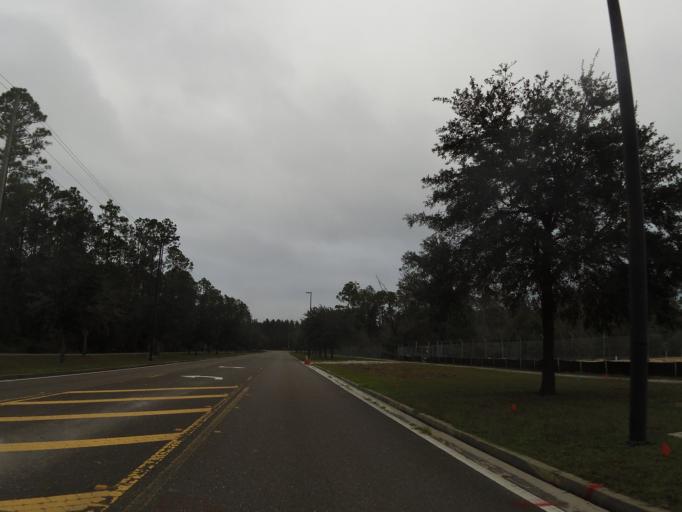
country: US
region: Florida
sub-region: Duval County
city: Baldwin
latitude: 30.2429
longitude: -81.8832
